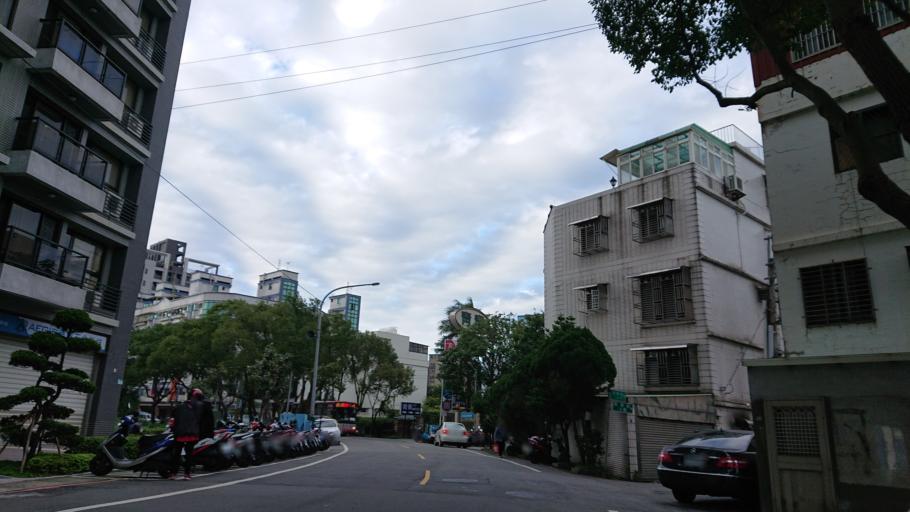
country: TW
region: Taiwan
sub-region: Taoyuan
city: Taoyuan
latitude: 24.9315
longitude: 121.3789
